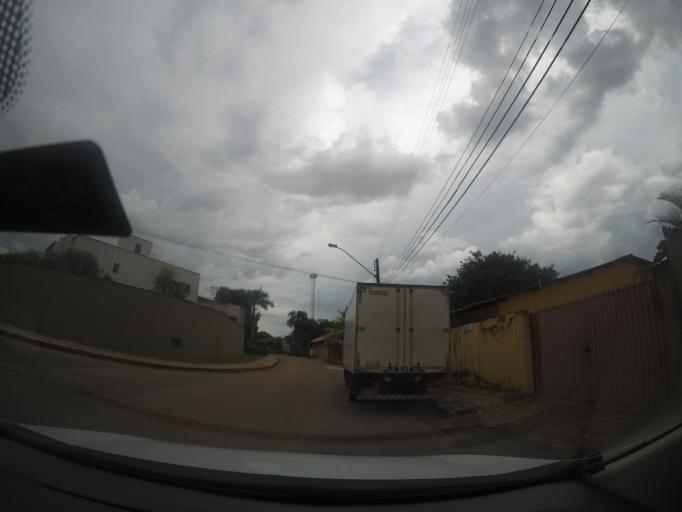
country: BR
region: Goias
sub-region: Goiania
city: Goiania
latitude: -16.6548
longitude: -49.2296
